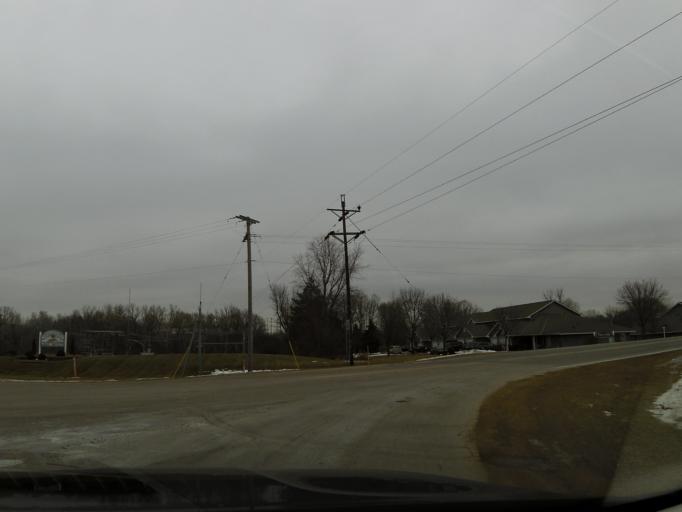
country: US
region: Minnesota
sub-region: Carver County
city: Watertown
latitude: 44.9585
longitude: -93.8389
